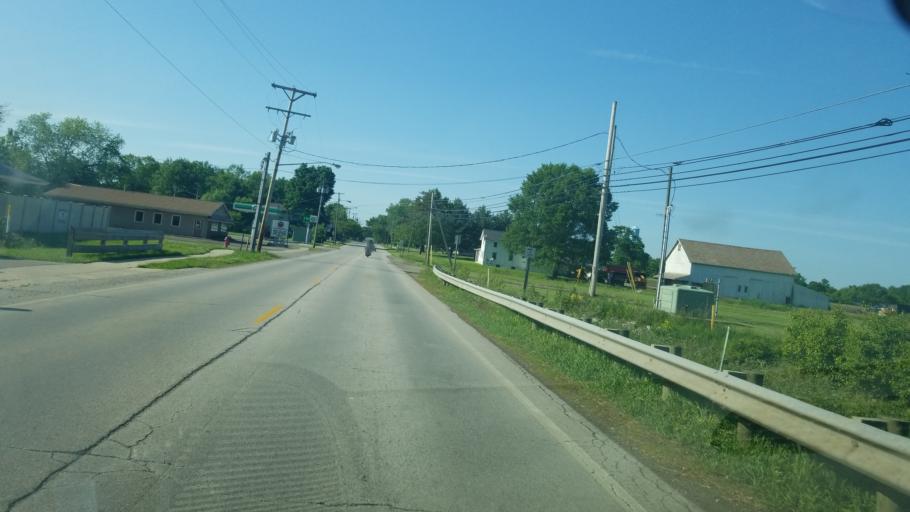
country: US
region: Ohio
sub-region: Wayne County
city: Creston
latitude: 40.9736
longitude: -81.8995
